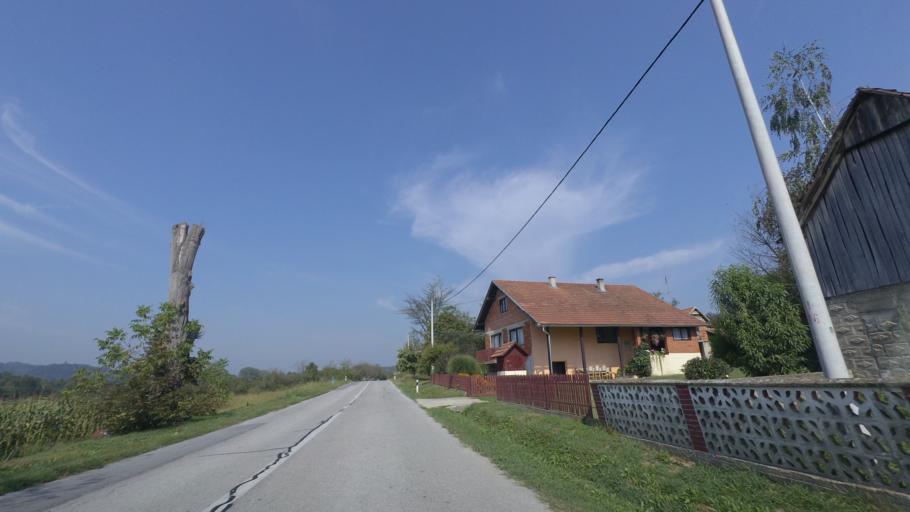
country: BA
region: Republika Srpska
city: Knezica
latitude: 45.2057
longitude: 16.6831
